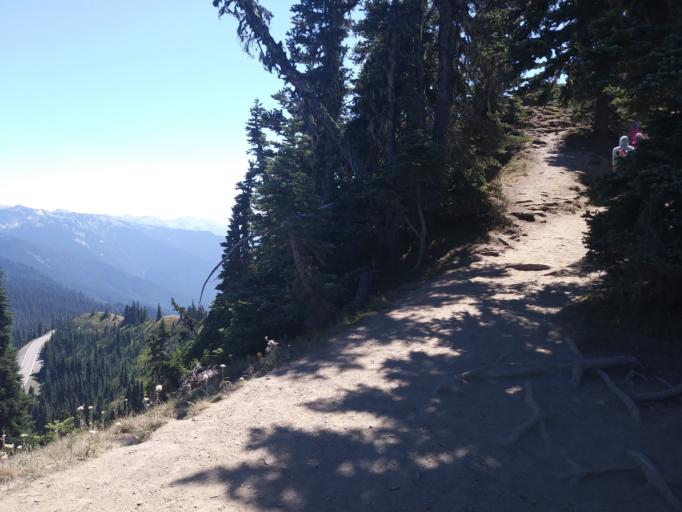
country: US
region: Washington
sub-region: Clallam County
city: Port Angeles
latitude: 47.9725
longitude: -123.4919
